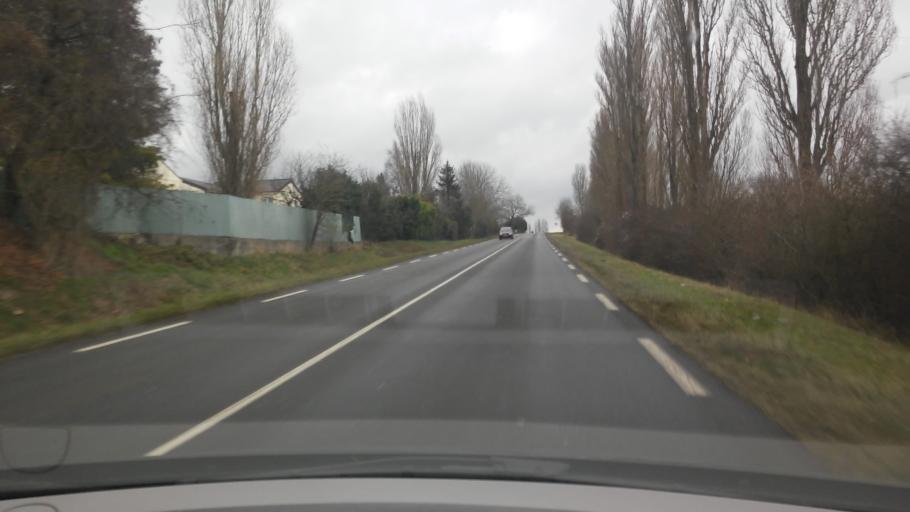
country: FR
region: Lorraine
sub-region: Departement de la Moselle
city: Retonfey
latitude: 49.1171
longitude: 6.2649
